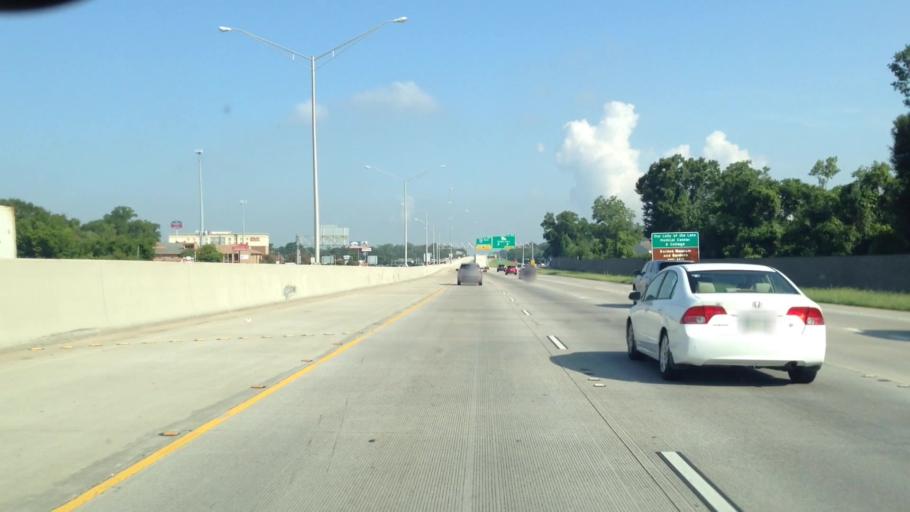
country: US
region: Louisiana
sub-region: East Baton Rouge Parish
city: Inniswold
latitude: 30.4026
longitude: -91.0950
